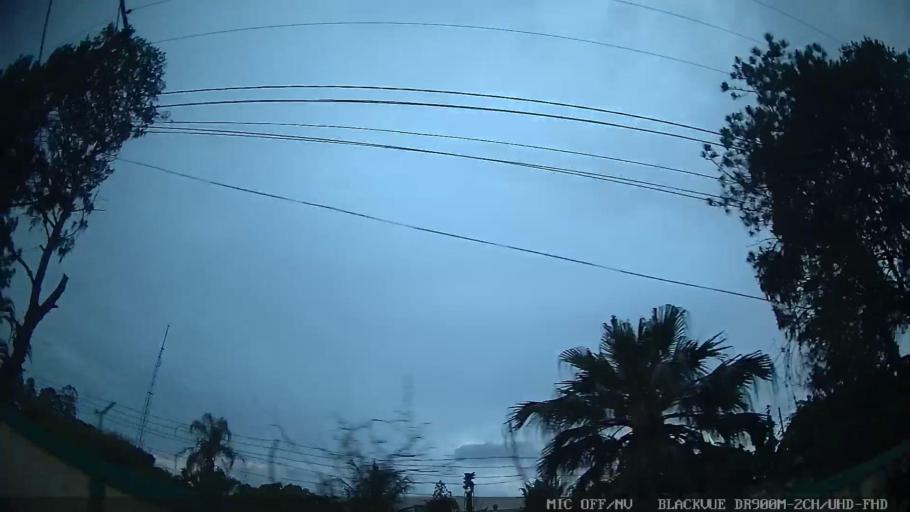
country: BR
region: Sao Paulo
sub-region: Louveira
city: Louveira
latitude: -23.1112
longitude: -46.9602
